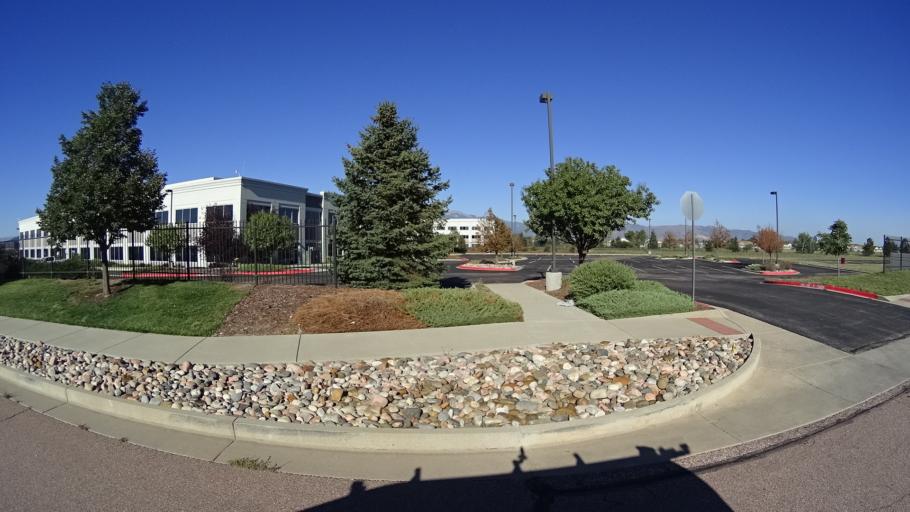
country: US
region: Colorado
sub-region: El Paso County
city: Cimarron Hills
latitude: 38.8172
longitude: -104.7252
